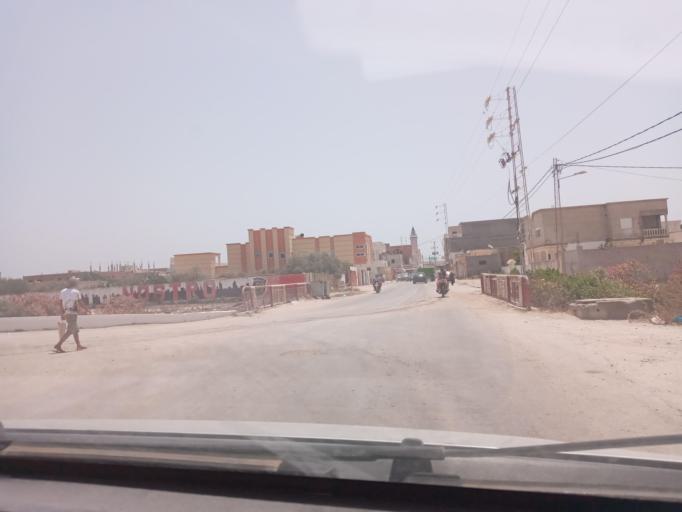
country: TN
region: Nabul
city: El Haouaria
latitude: 37.0132
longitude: 10.9522
